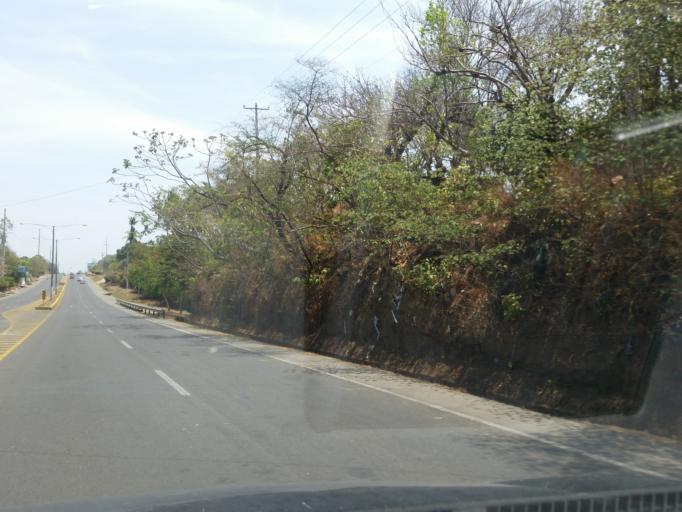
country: NI
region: Masaya
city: Masaya
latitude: 11.9728
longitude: -86.0260
